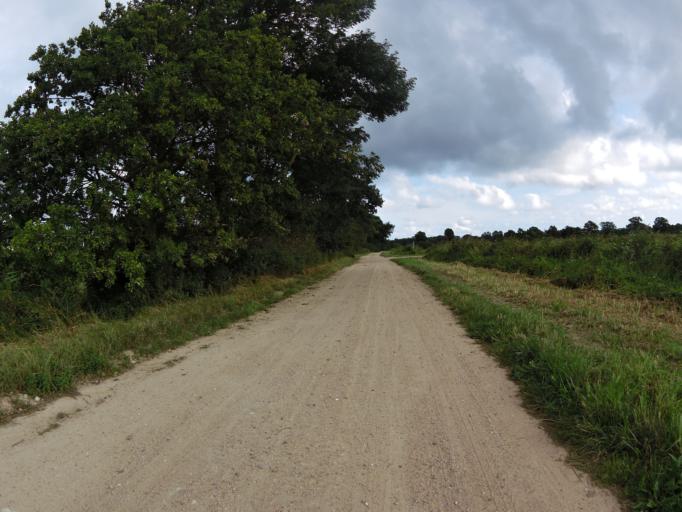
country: DE
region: Mecklenburg-Vorpommern
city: Loddin
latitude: 53.9857
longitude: 14.0616
